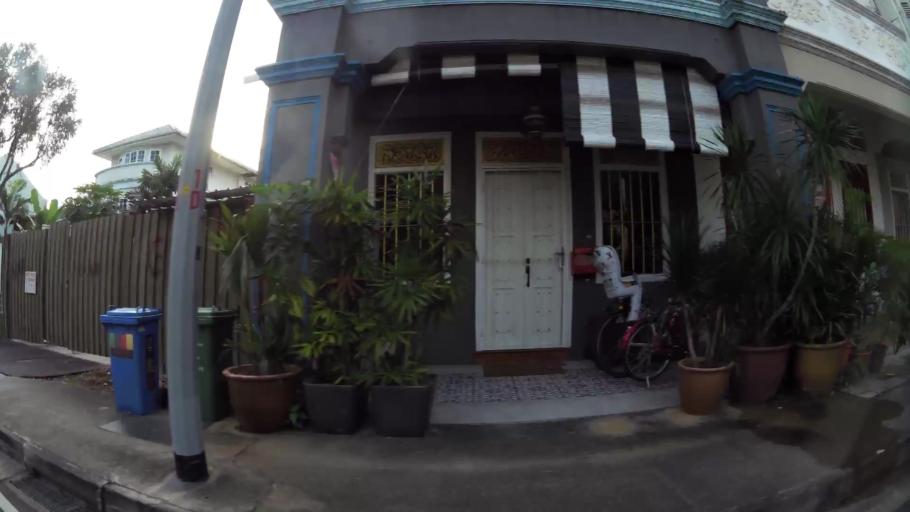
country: SG
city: Singapore
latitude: 1.3113
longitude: 103.9041
